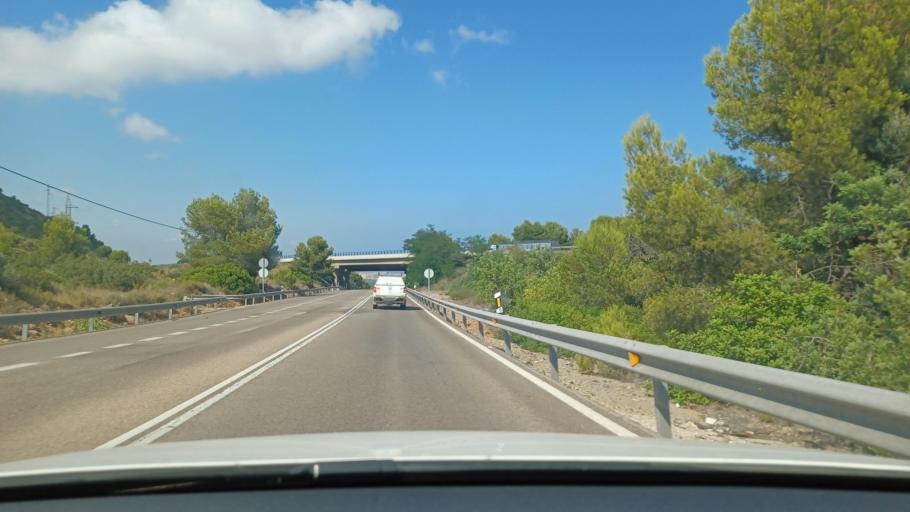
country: ES
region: Valencia
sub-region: Provincia de Castello
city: Orpesa/Oropesa del Mar
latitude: 40.0805
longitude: 0.1168
